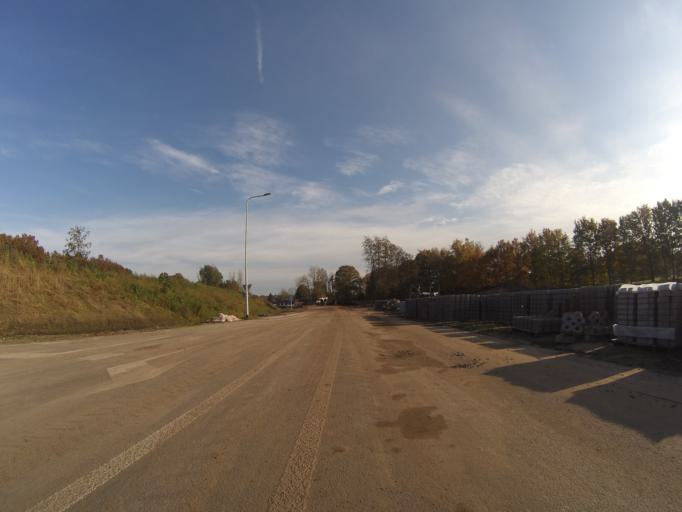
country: NL
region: Gelderland
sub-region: Gemeente Barneveld
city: Voorthuizen
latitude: 52.1934
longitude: 5.6034
